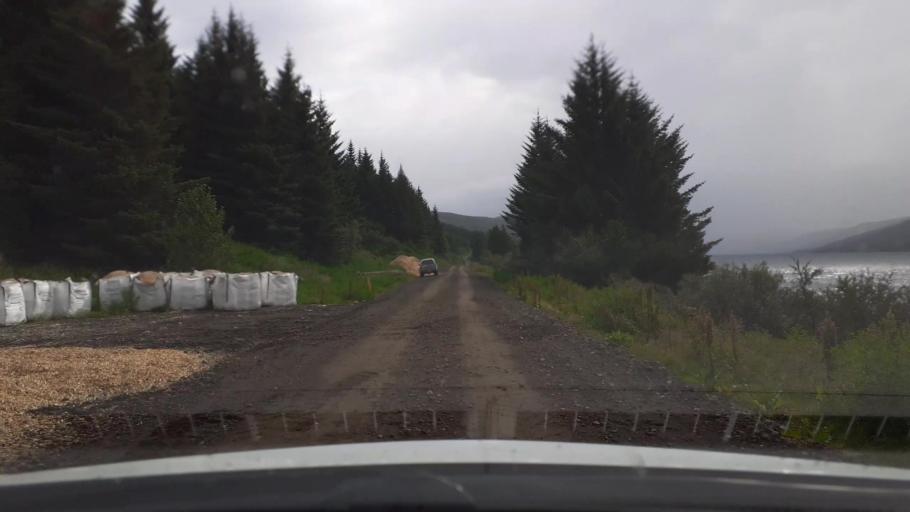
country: IS
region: Capital Region
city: Mosfellsbaer
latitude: 64.5189
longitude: -21.4306
